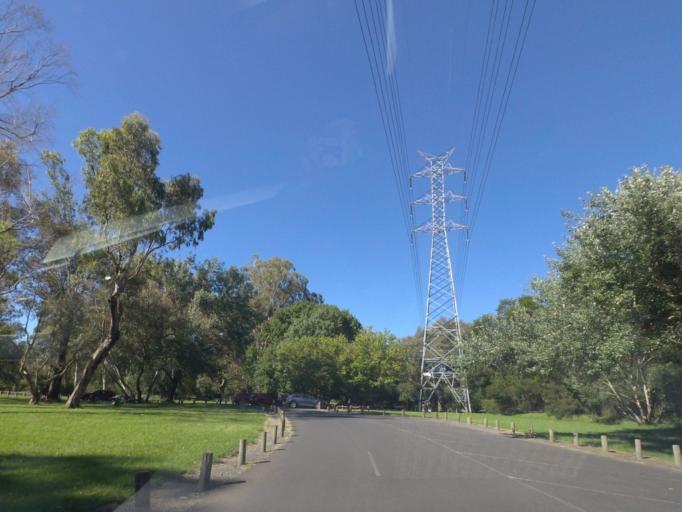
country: AU
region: Victoria
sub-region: Manningham
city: Bulleen
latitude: -37.7579
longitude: 145.0813
